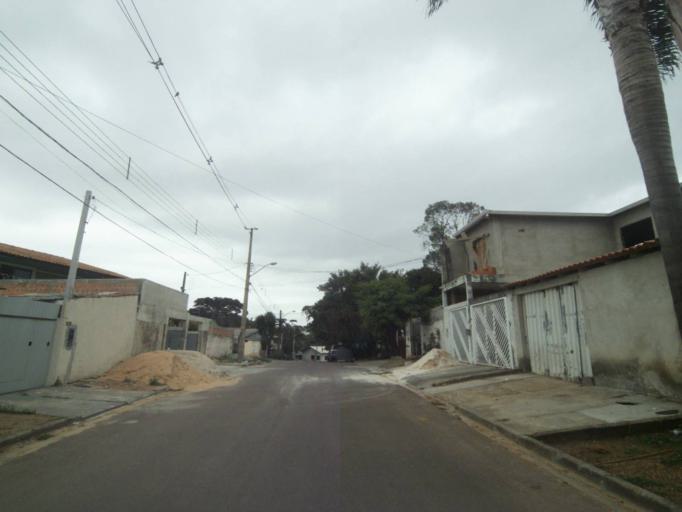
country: BR
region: Parana
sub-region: Sao Jose Dos Pinhais
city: Sao Jose dos Pinhais
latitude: -25.5466
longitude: -49.2487
